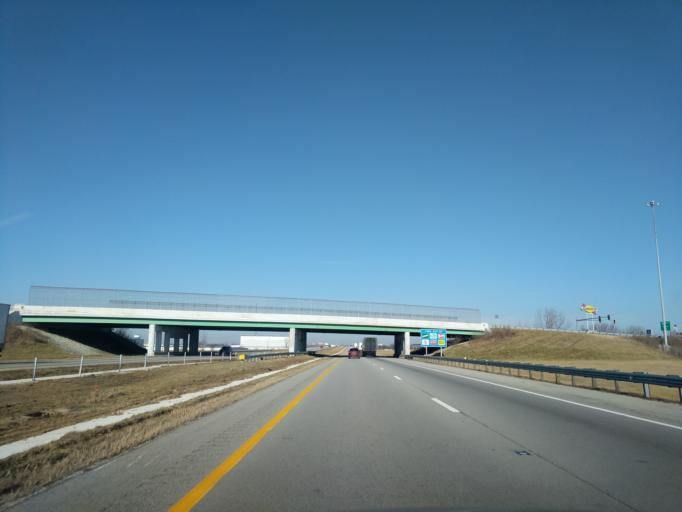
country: US
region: Ohio
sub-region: Shelby County
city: Sidney
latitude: 40.2669
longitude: -84.1831
